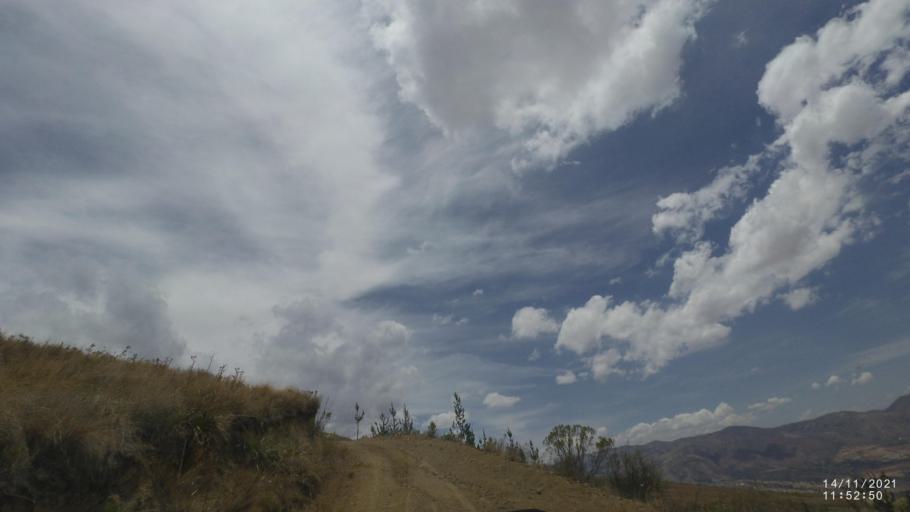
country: BO
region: Cochabamba
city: Colomi
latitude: -17.3637
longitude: -65.9824
